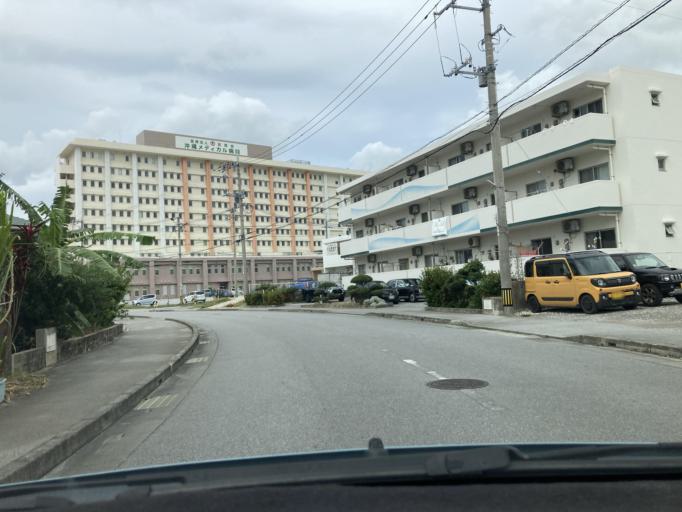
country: JP
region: Okinawa
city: Ginowan
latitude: 26.1863
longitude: 127.7770
